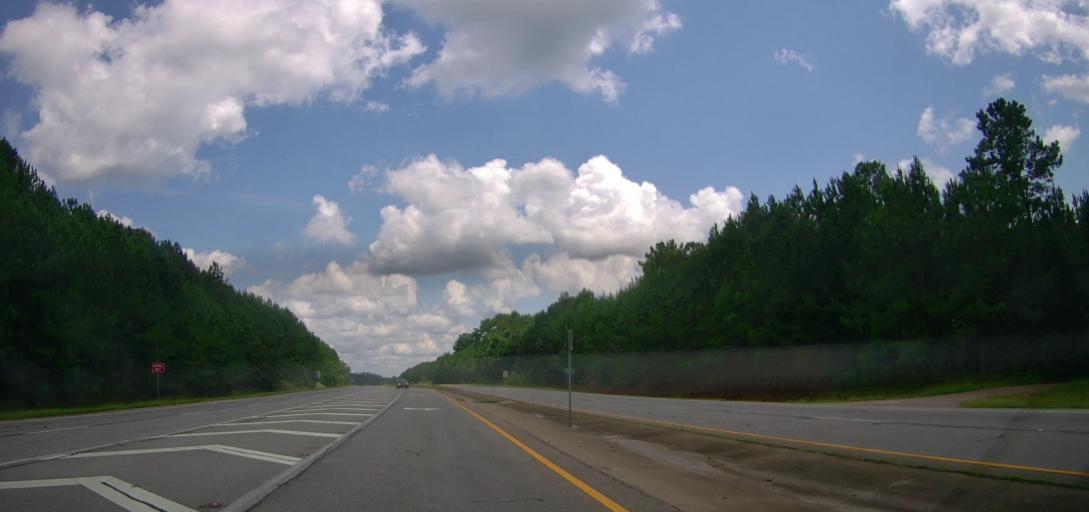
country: US
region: Georgia
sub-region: Heard County
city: Franklin
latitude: 33.2650
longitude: -85.0726
